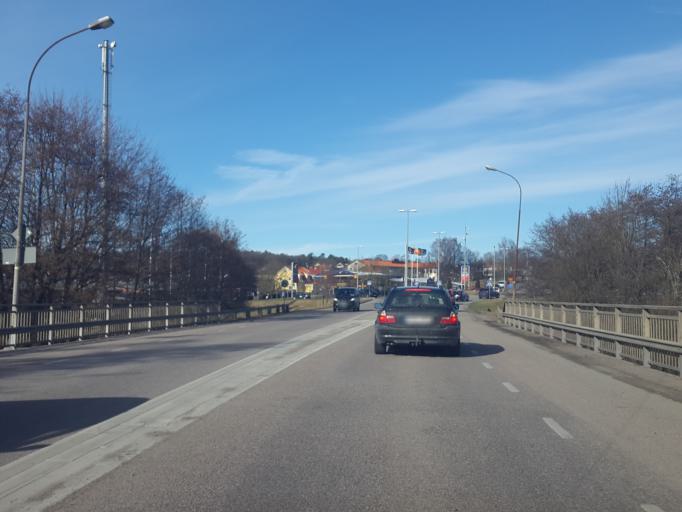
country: SE
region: Vaestra Goetaland
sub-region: Alingsas Kommun
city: Alingsas
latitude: 57.9335
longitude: 12.5443
